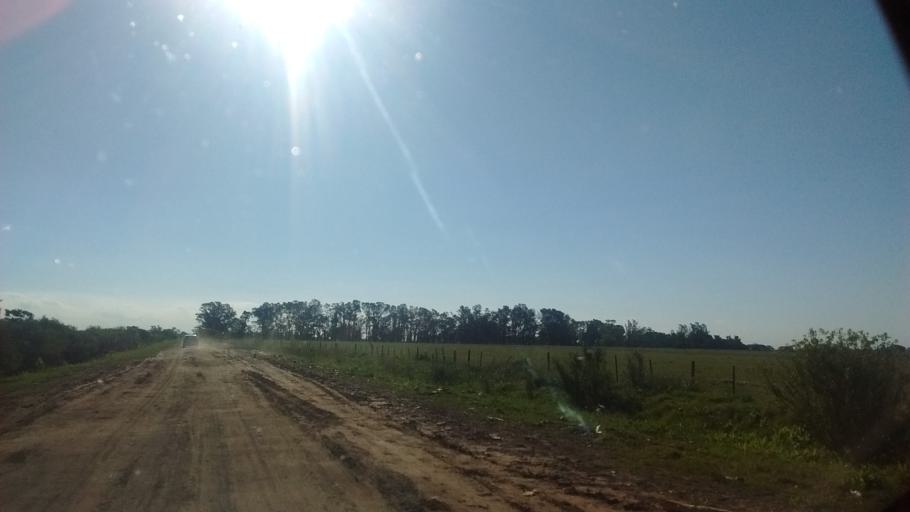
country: AR
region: Santa Fe
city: Funes
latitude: -32.8934
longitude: -60.7981
